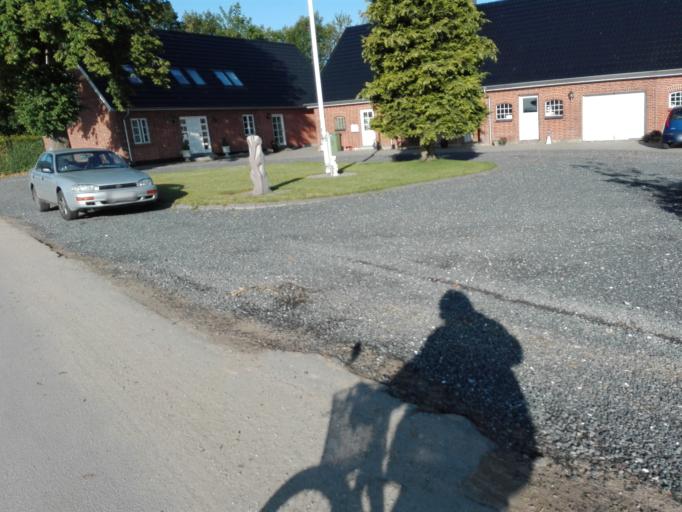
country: DK
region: Central Jutland
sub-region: Arhus Kommune
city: Marslet
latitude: 56.0780
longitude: 10.1442
